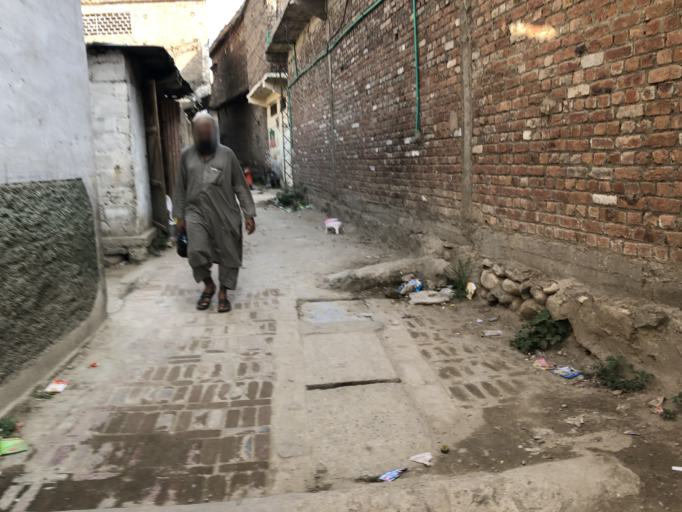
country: PK
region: Khyber Pakhtunkhwa
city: Daggar
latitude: 34.5971
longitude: 72.4513
